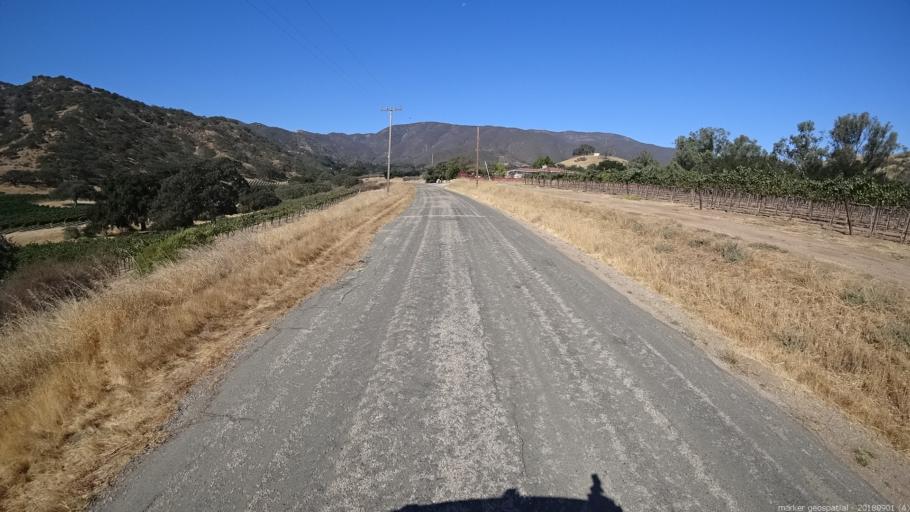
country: US
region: California
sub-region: Monterey County
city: Soledad
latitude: 36.3364
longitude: -121.3497
